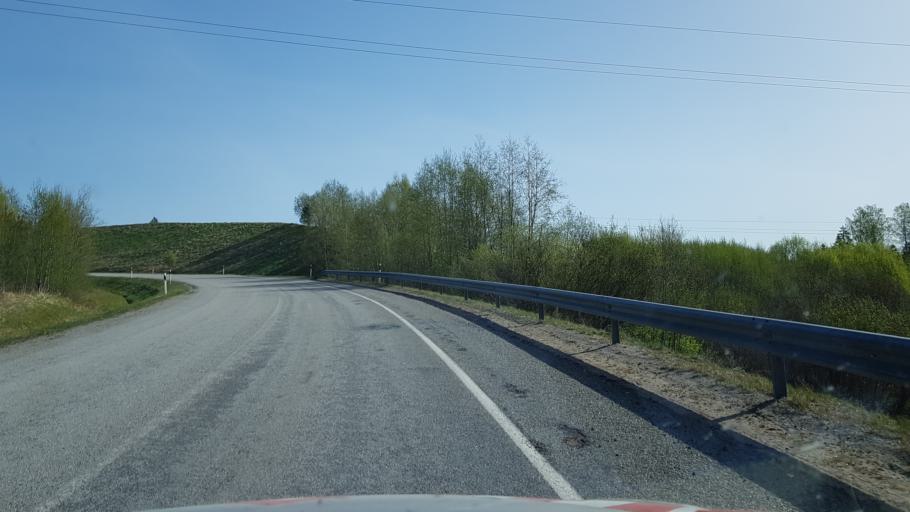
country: EE
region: Viljandimaa
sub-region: Abja vald
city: Abja-Paluoja
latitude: 58.1403
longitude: 25.3751
